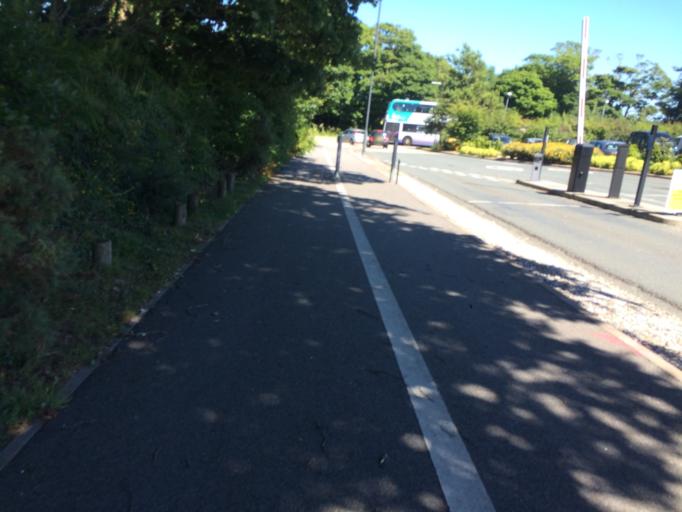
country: GB
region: England
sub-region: Cornwall
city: Penryn
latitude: 50.1717
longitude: -5.1249
